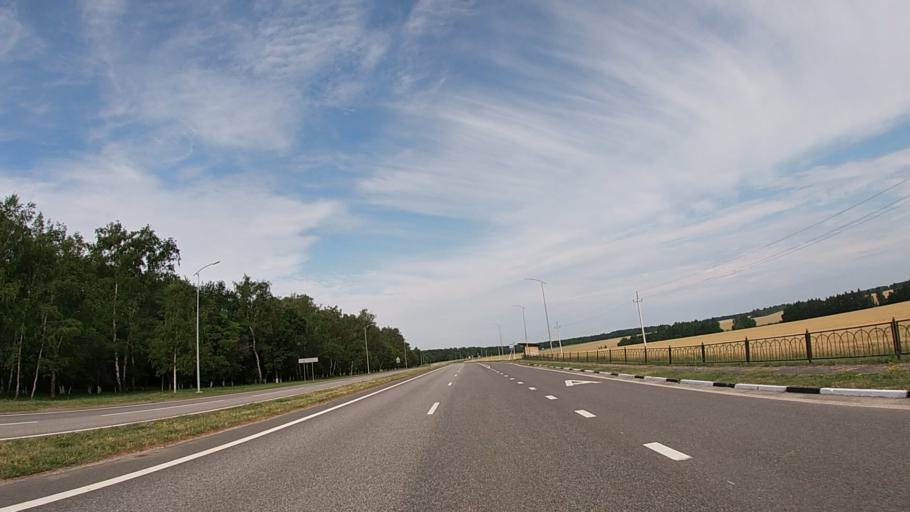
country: RU
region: Belgorod
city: Borisovka
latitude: 50.7506
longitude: 35.9823
